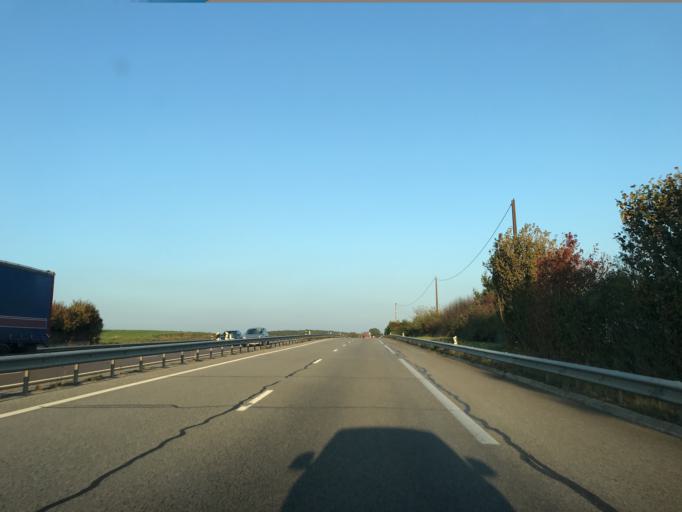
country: FR
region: Lower Normandy
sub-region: Departement de l'Orne
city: Valframbert
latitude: 48.4695
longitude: 0.1724
